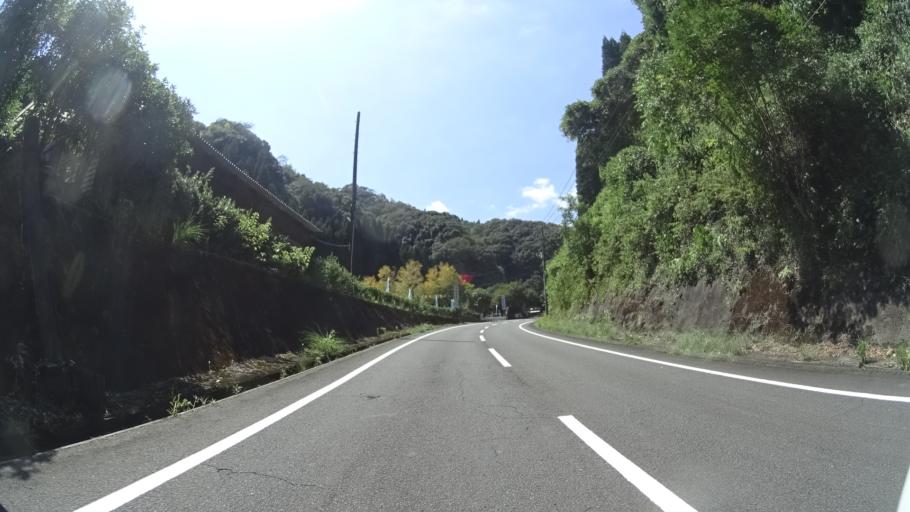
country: JP
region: Kagoshima
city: Kokubu-matsuki
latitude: 31.8289
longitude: 130.7361
